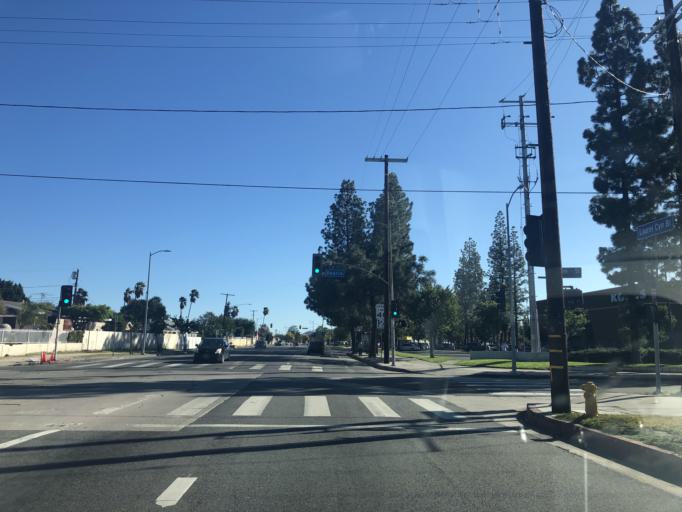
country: US
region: California
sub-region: Los Angeles County
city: North Hollywood
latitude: 34.2262
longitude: -118.3978
